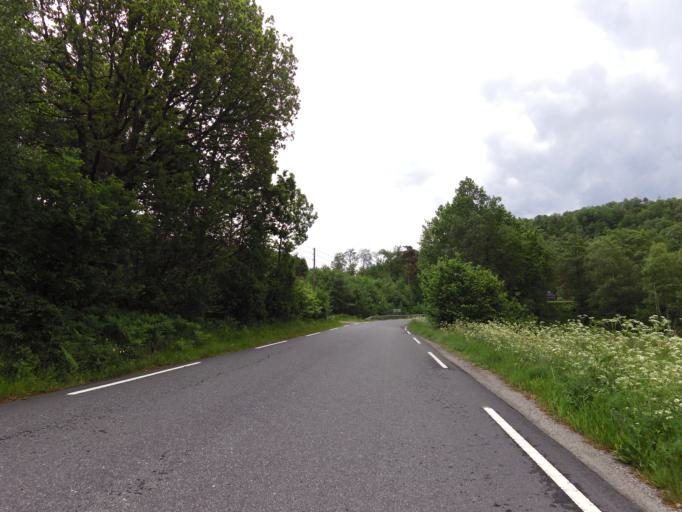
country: NO
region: Vest-Agder
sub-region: Lyngdal
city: Lyngdal
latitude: 58.1121
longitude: 6.9549
